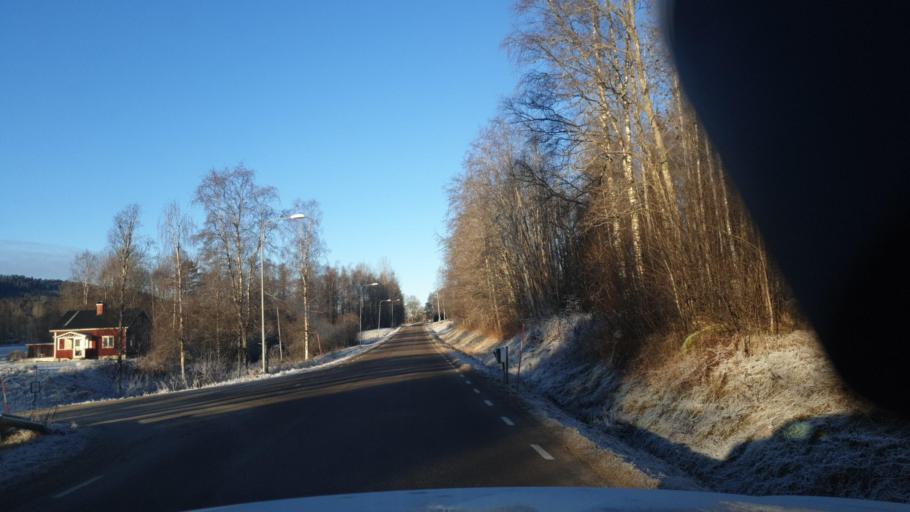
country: SE
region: Vaermland
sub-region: Arvika Kommun
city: Arvika
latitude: 59.7572
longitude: 12.7973
